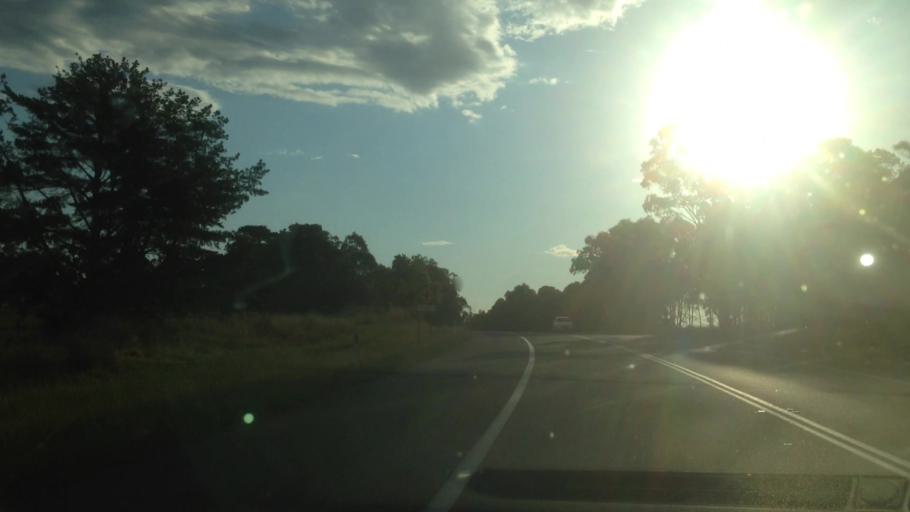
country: AU
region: New South Wales
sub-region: Cessnock
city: Heddon Greta
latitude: -32.8308
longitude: 151.5153
